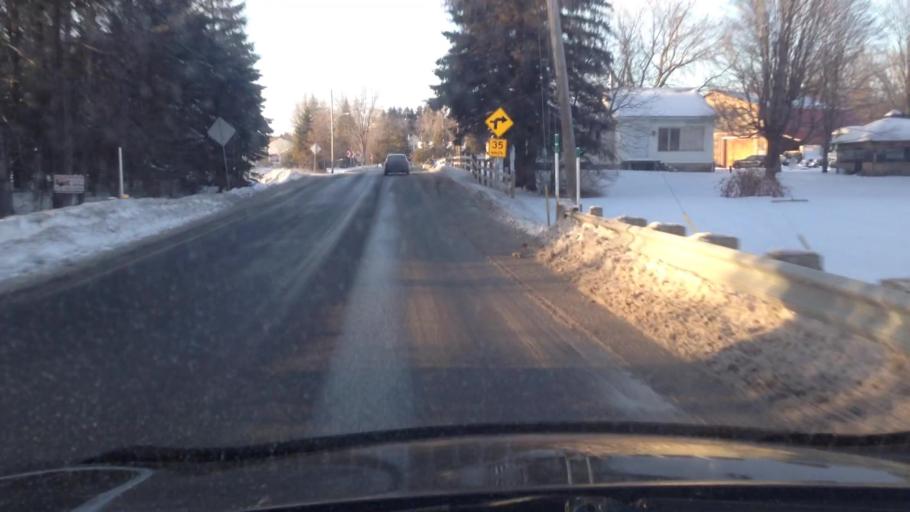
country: CA
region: Quebec
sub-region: Lanaudiere
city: Sainte-Julienne
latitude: 45.9149
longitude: -73.7373
